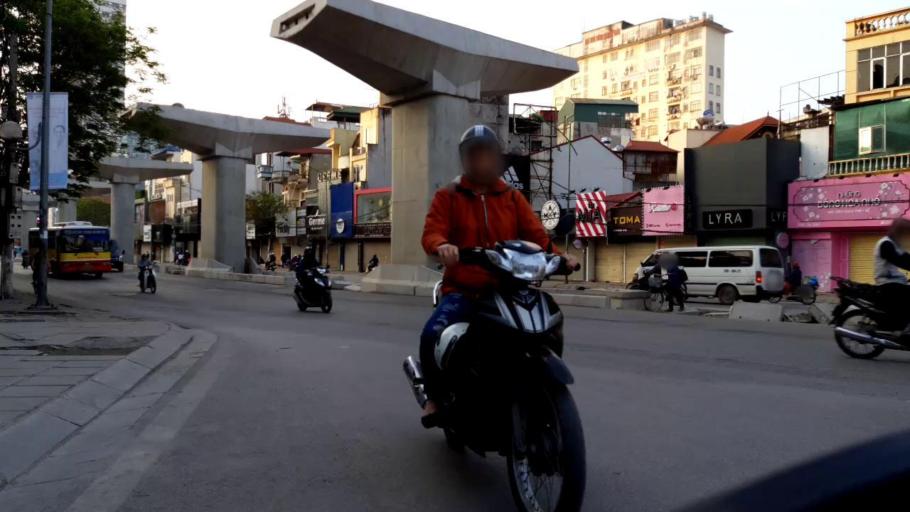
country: VN
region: Ha Noi
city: Cau Giay
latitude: 21.0337
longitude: 105.7977
